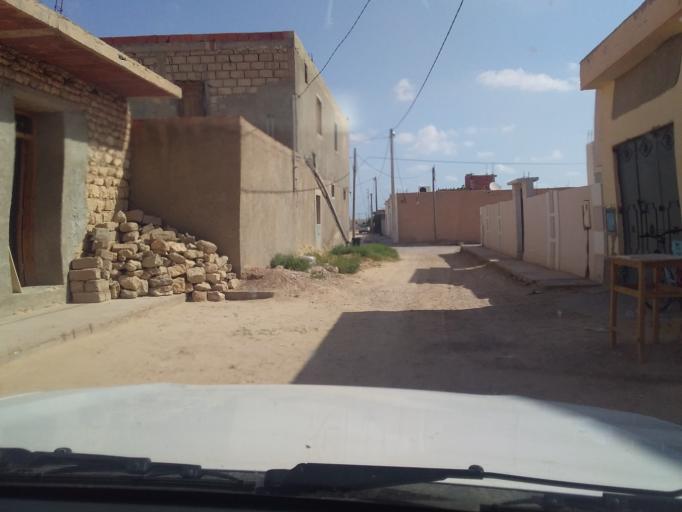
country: TN
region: Madanin
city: Medenine
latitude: 33.5816
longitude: 10.3249
